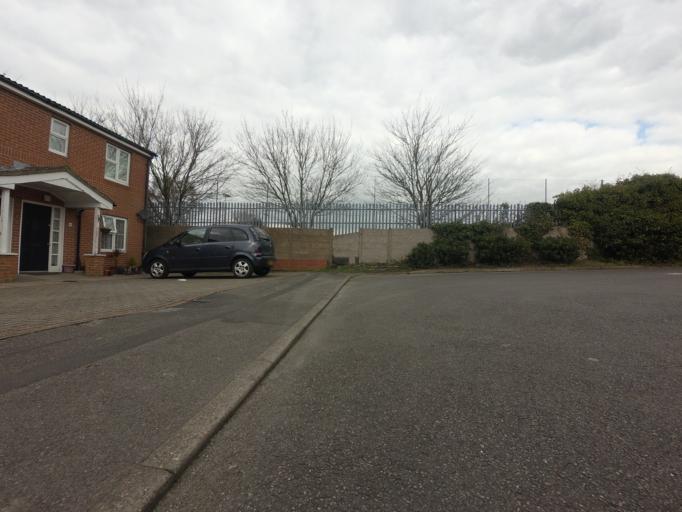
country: GB
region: England
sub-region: Kent
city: Swanley
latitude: 51.3966
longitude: 0.1675
